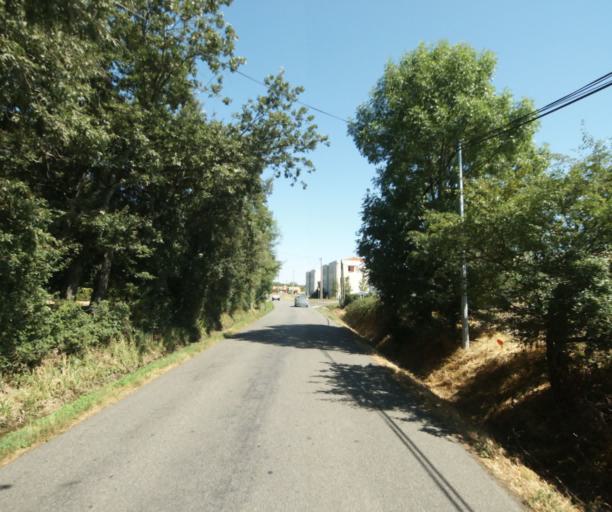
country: FR
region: Midi-Pyrenees
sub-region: Departement de la Haute-Garonne
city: Revel
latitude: 43.4701
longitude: 1.9922
